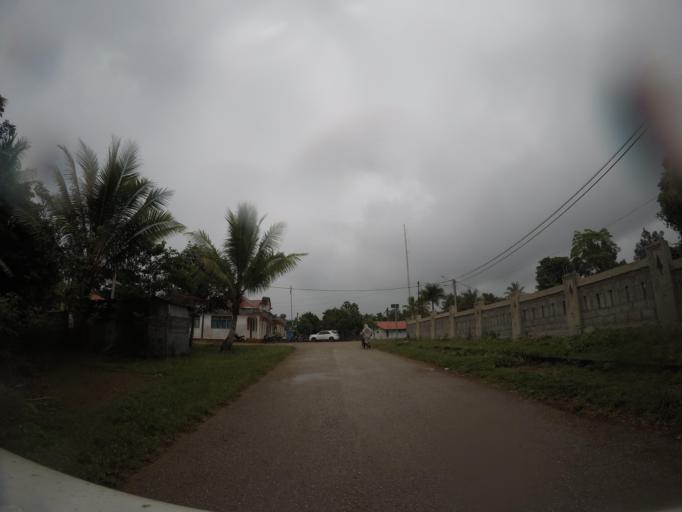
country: TL
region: Lautem
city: Lospalos
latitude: -8.5250
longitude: 126.9950
